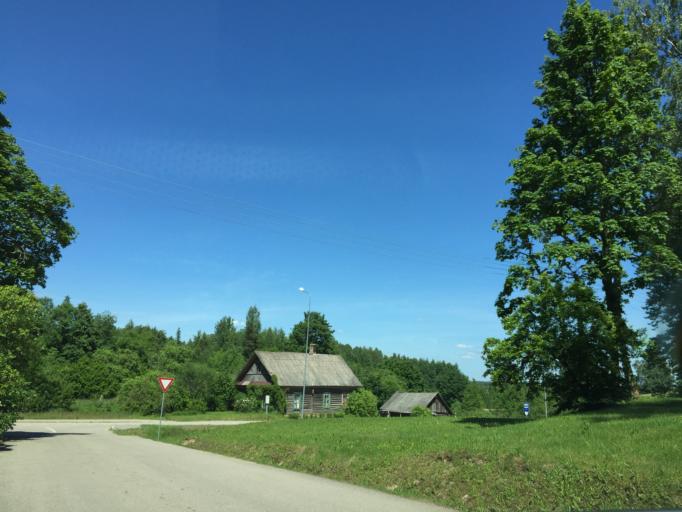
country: LV
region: Preilu Rajons
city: Jaunaglona
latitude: 56.2347
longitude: 27.2302
